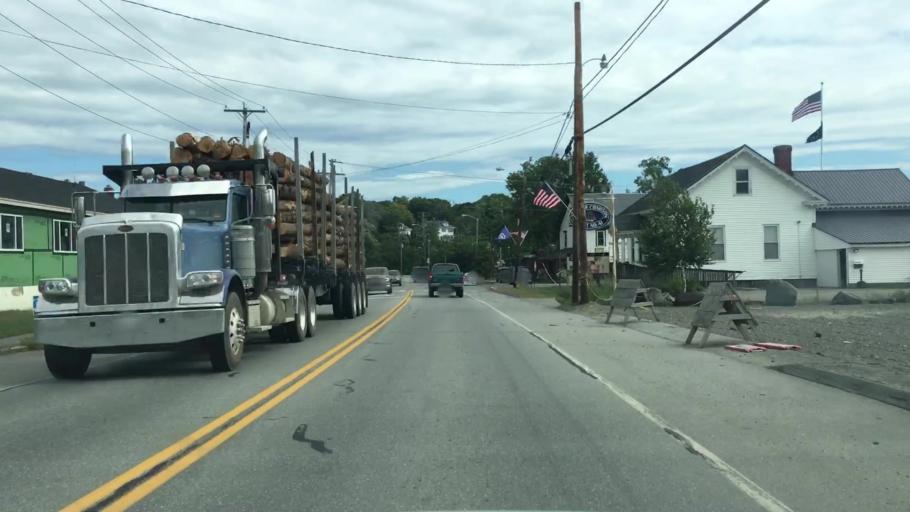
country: US
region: Maine
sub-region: Piscataquis County
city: Milo
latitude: 45.2504
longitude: -68.9895
